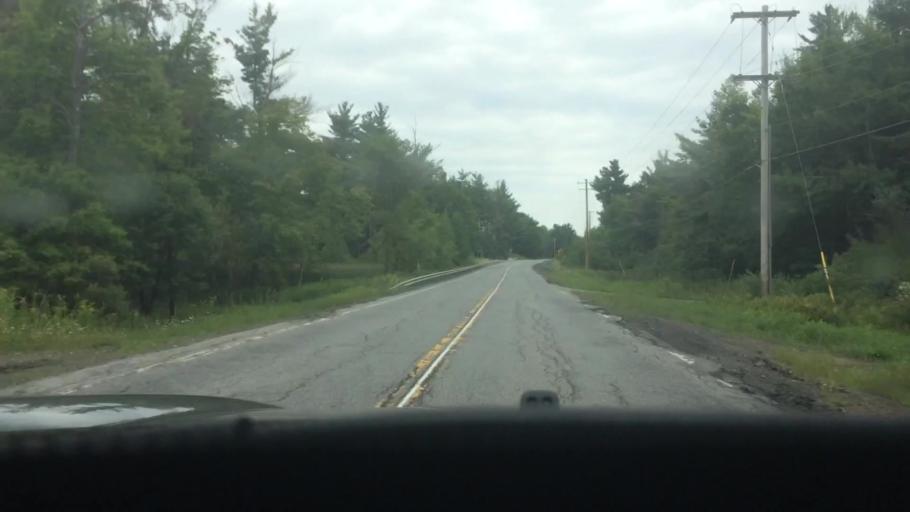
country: US
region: New York
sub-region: St. Lawrence County
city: Hannawa Falls
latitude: 44.5479
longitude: -74.9468
